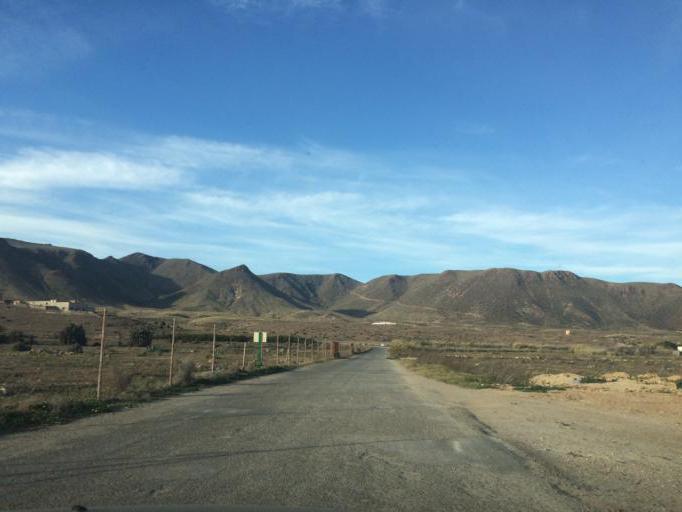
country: ES
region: Andalusia
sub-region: Provincia de Almeria
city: San Jose
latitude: 36.8040
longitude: -2.0643
